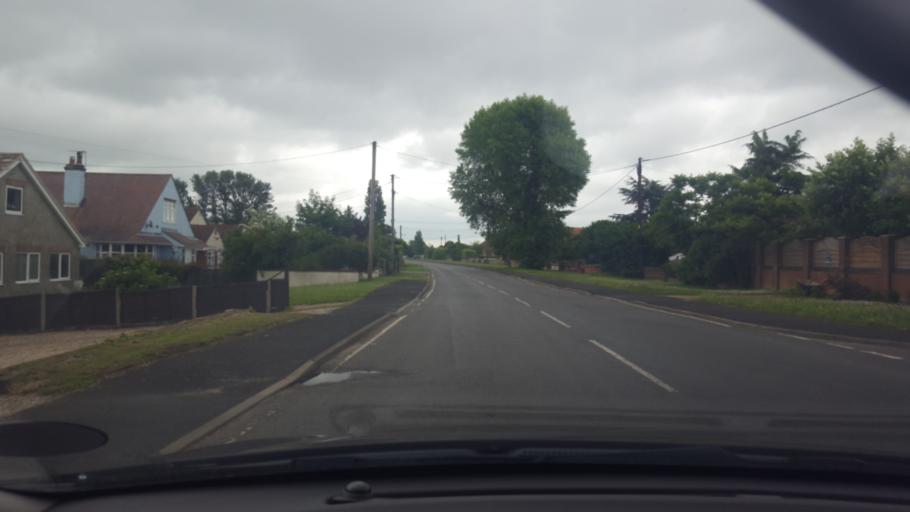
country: GB
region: England
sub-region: Essex
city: Brightlingsea
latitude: 51.7938
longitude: 1.0360
